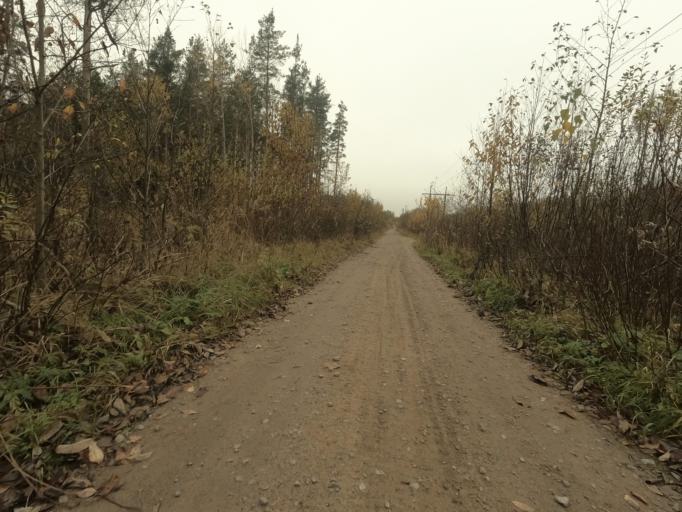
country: RU
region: Leningrad
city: Pavlovo
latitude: 59.7684
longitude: 30.9315
